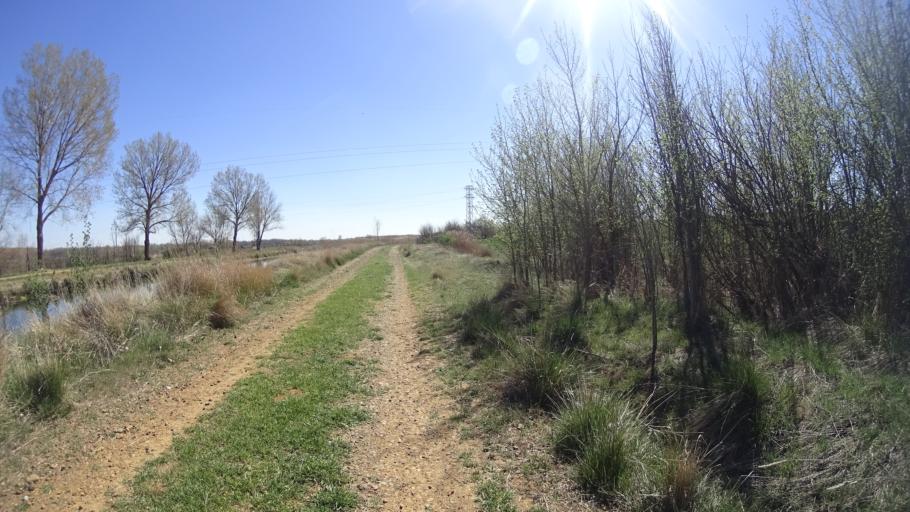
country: ES
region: Castille and Leon
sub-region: Provincia de Burgos
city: Melgar de Fernamental
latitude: 42.4121
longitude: -4.2786
